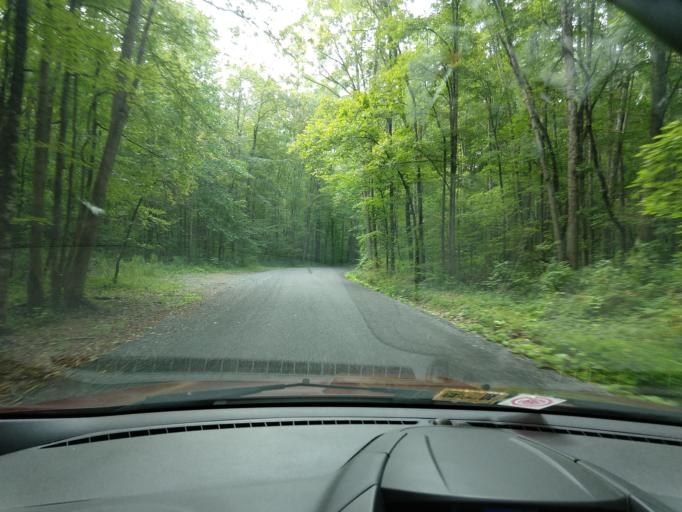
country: US
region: Virginia
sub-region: City of Covington
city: Covington
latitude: 37.9235
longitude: -80.0751
